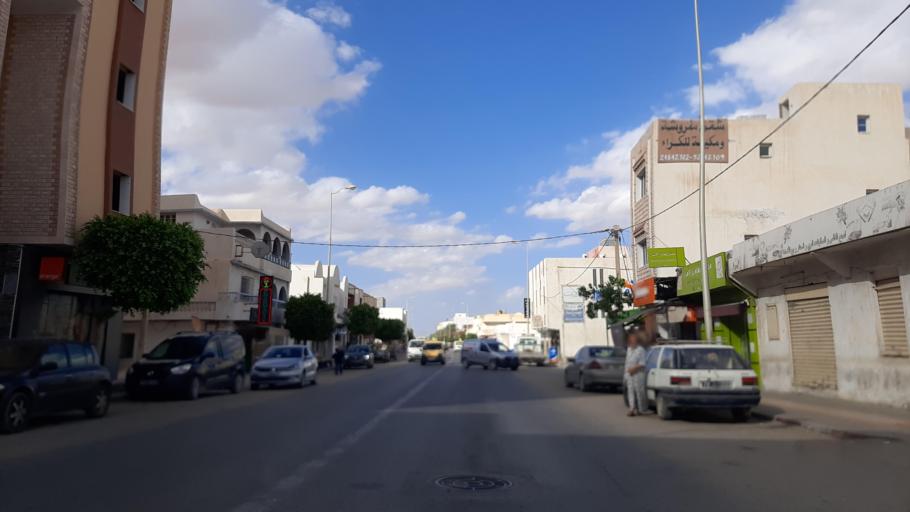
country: TN
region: Tataouine
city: Tataouine
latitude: 32.9326
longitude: 10.4508
